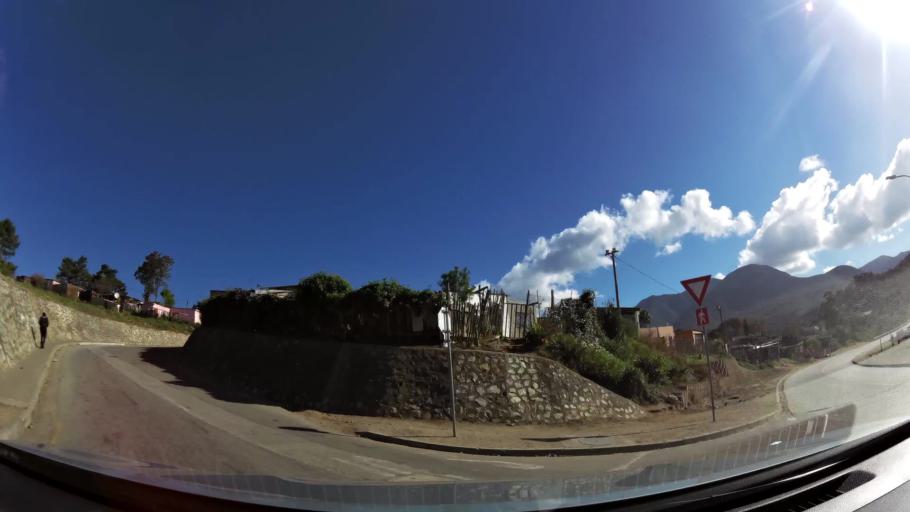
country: ZA
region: Western Cape
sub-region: Eden District Municipality
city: George
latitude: -33.9413
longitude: 22.4107
